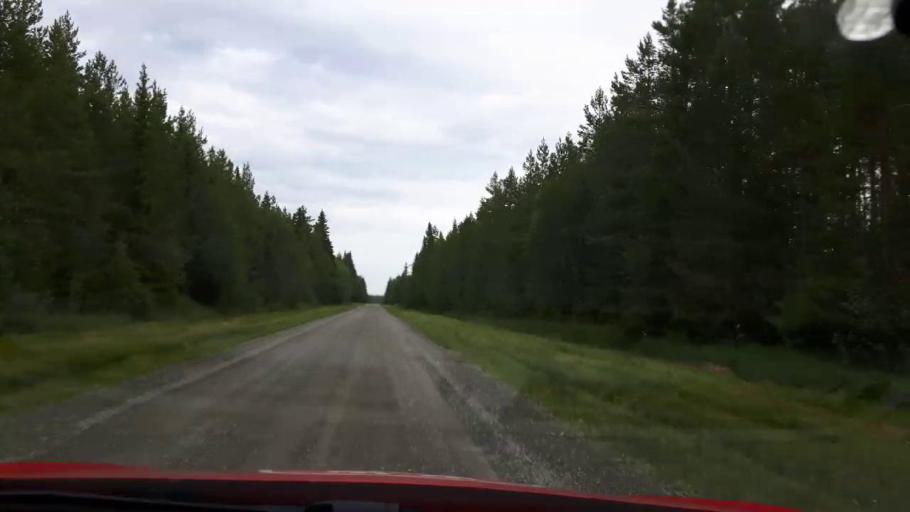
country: SE
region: Jaemtland
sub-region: Stroemsunds Kommun
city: Stroemsund
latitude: 63.7263
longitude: 15.5437
